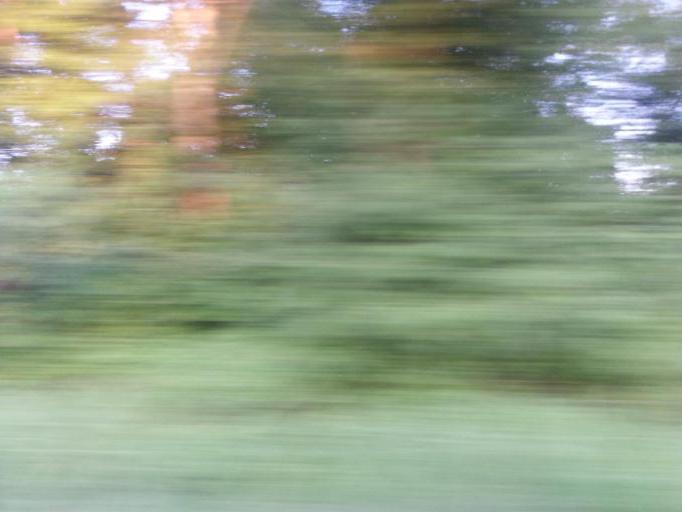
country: US
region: Tennessee
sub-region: Monroe County
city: Sweetwater
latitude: 35.6446
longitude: -84.4288
